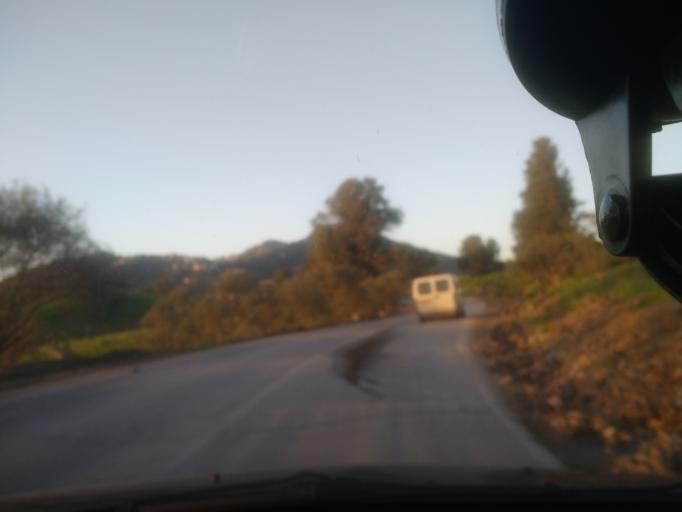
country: DZ
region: Boumerdes
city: Makouda
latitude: 36.7663
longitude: 4.0649
